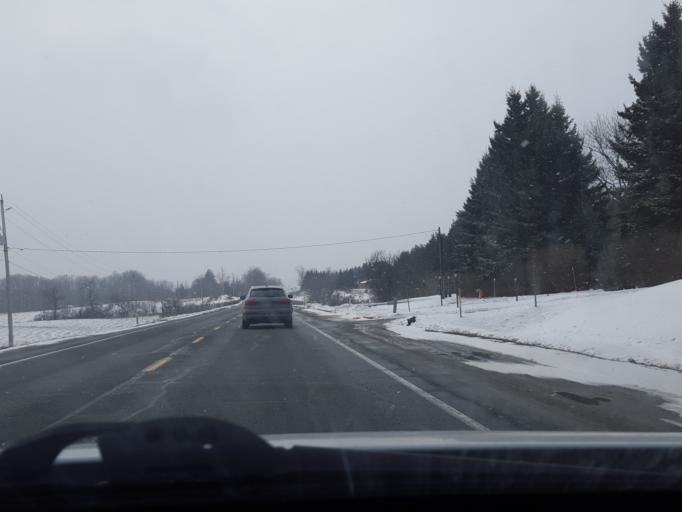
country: CA
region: Ontario
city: Markham
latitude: 44.0082
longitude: -79.2548
